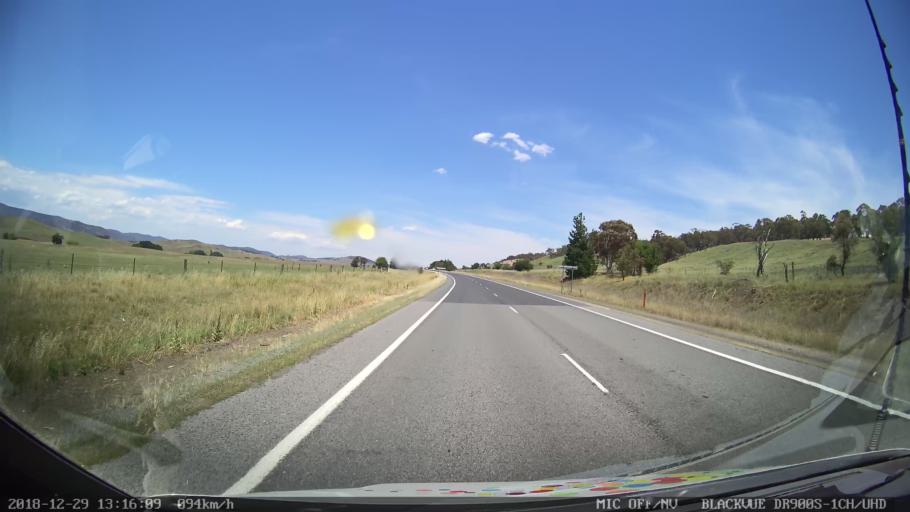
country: AU
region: Australian Capital Territory
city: Macarthur
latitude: -35.7193
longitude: 149.1585
